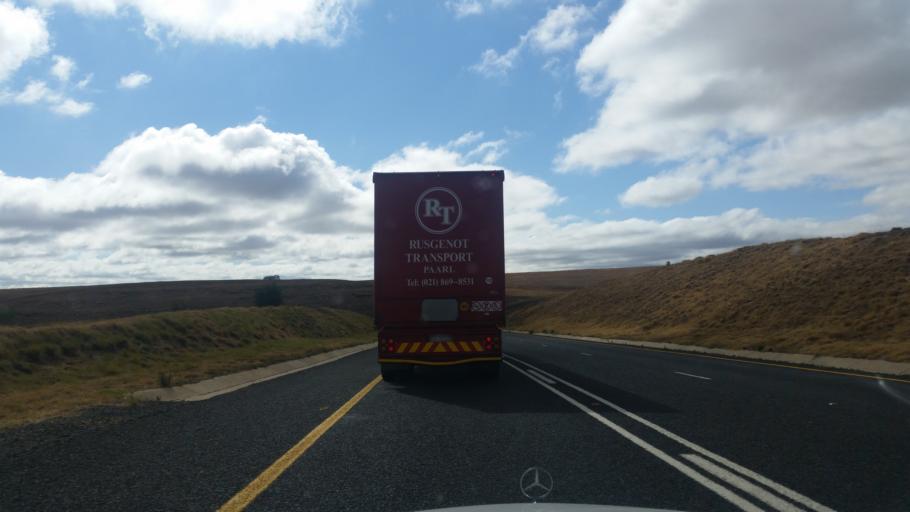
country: ZA
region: Orange Free State
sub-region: Thabo Mofutsanyana District Municipality
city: Phuthaditjhaba
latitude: -28.2716
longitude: 28.8560
